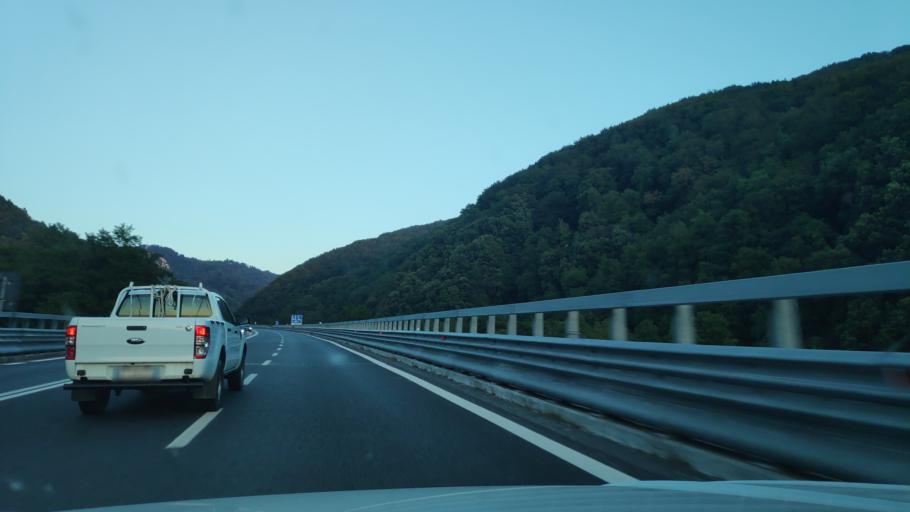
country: IT
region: Calabria
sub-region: Provincia di Reggio Calabria
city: Amato
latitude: 38.4059
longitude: 16.1514
